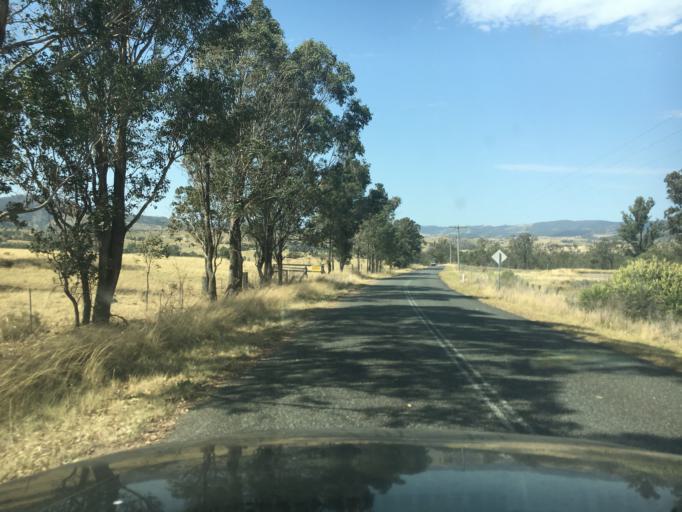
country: AU
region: New South Wales
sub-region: Singleton
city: Singleton
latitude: -32.5096
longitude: 151.3011
